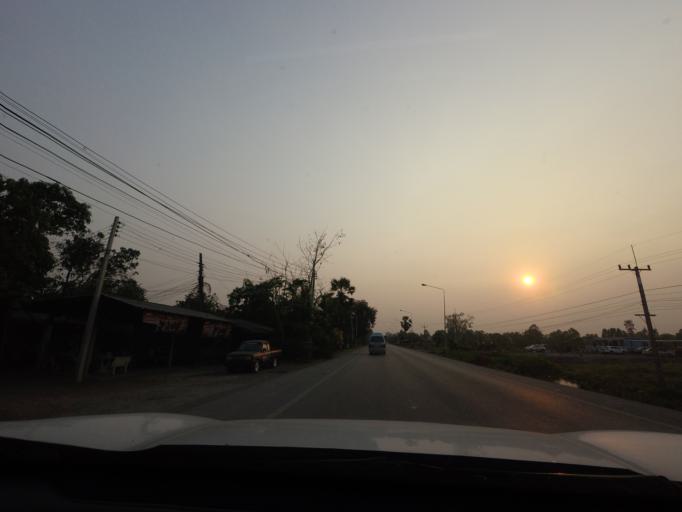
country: TH
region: Nakhon Nayok
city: Ban Na
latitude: 14.1884
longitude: 101.0704
